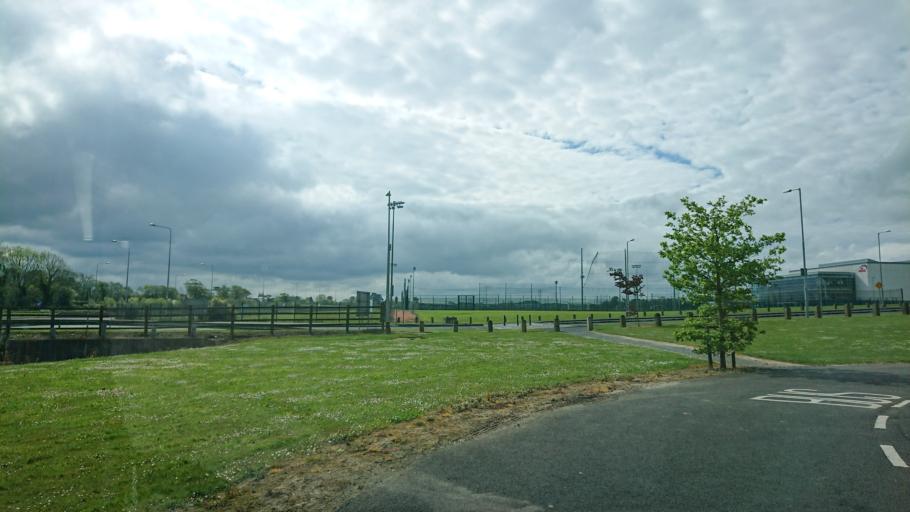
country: IE
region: Munster
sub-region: Waterford
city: Waterford
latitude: 52.2539
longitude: -7.1800
